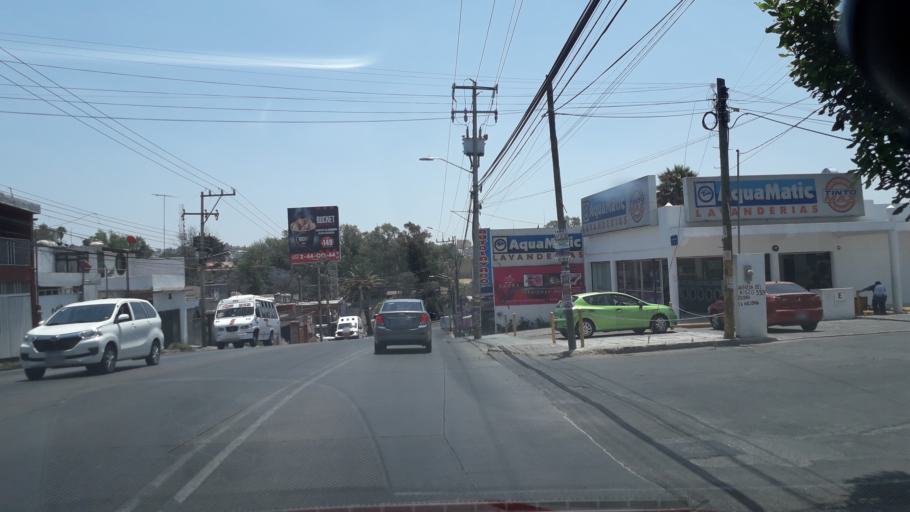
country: MX
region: Puebla
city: Puebla
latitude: 19.0127
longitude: -98.1911
